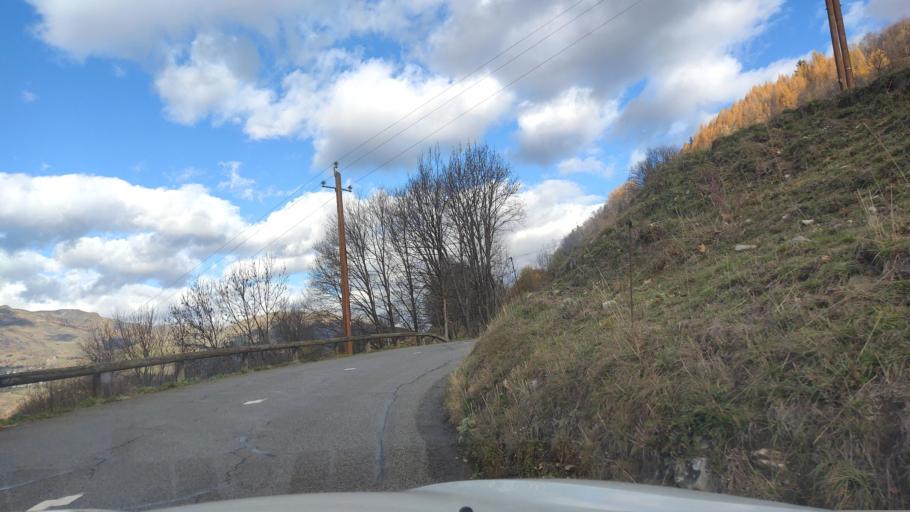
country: FR
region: Rhone-Alpes
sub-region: Departement de la Savoie
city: Saint-Jean-de-Maurienne
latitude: 45.2195
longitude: 6.3218
